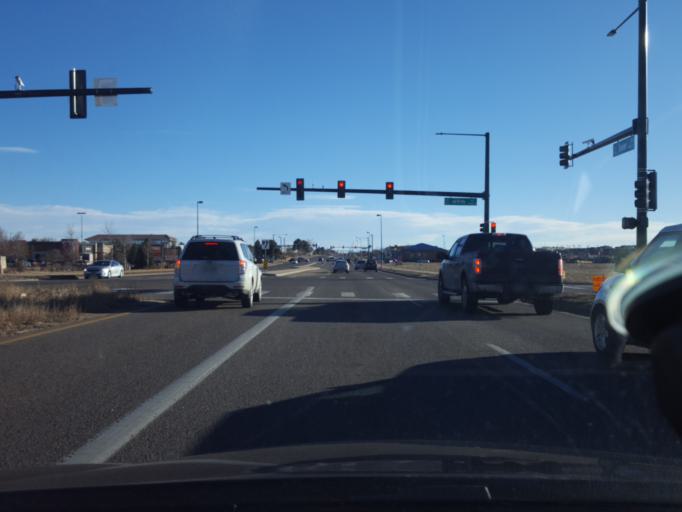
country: US
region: Colorado
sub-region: Adams County
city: Aurora
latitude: 39.7862
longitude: -104.7722
